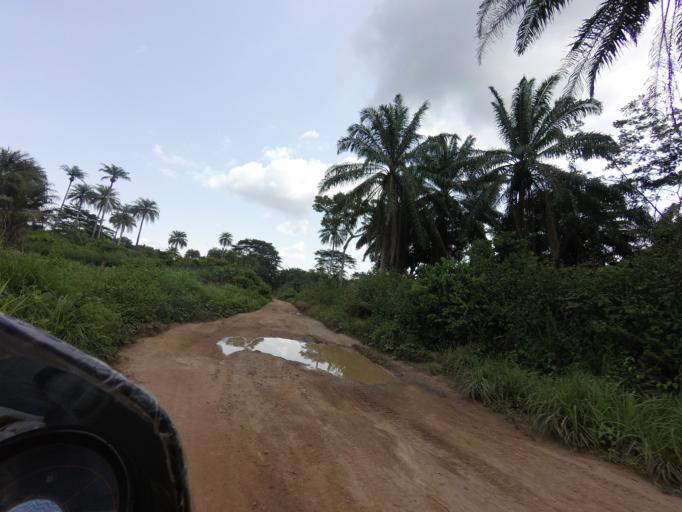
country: SL
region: Eastern Province
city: Manowa
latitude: 8.1538
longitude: -10.7560
